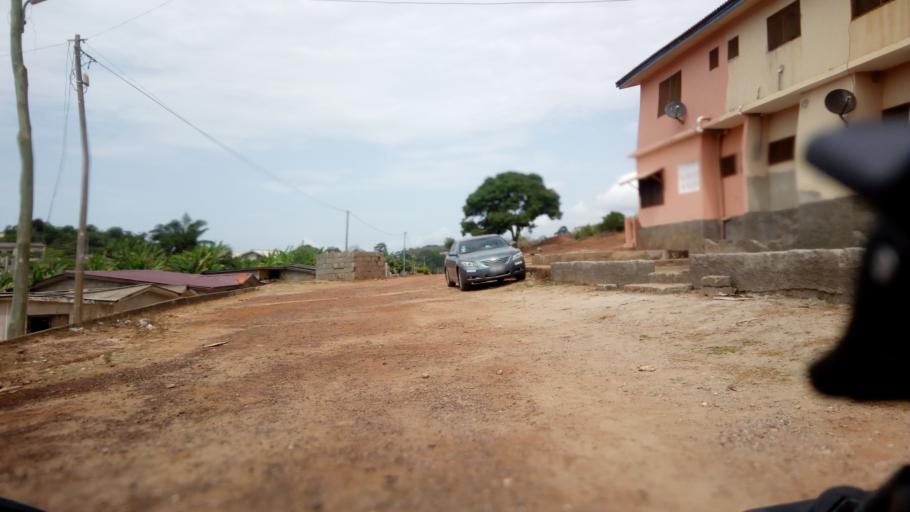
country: GH
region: Central
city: Cape Coast
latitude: 5.1077
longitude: -1.2757
